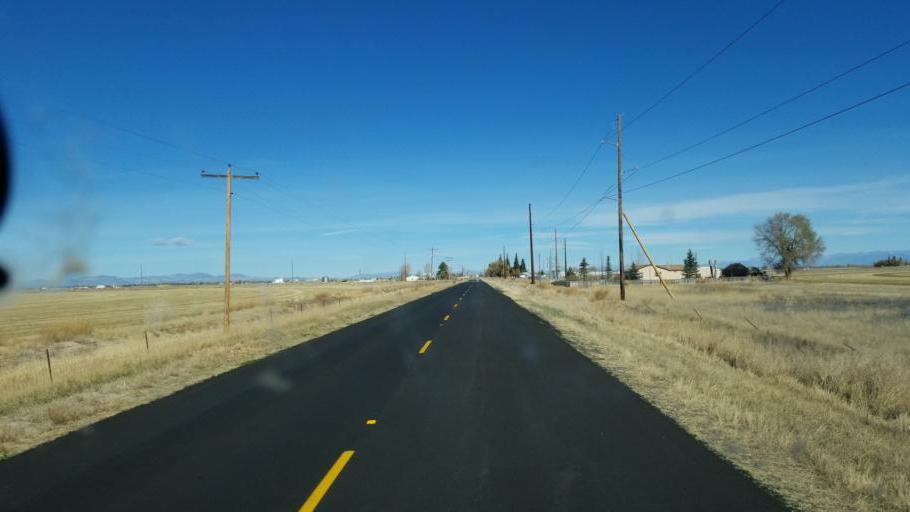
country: US
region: Colorado
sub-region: Rio Grande County
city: Monte Vista
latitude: 37.5412
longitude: -106.0942
